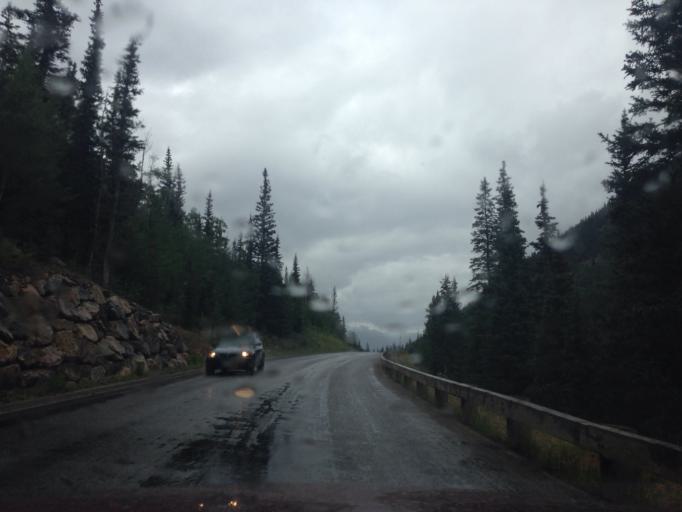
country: US
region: Colorado
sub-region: Clear Creek County
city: Georgetown
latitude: 39.6419
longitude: -105.7079
